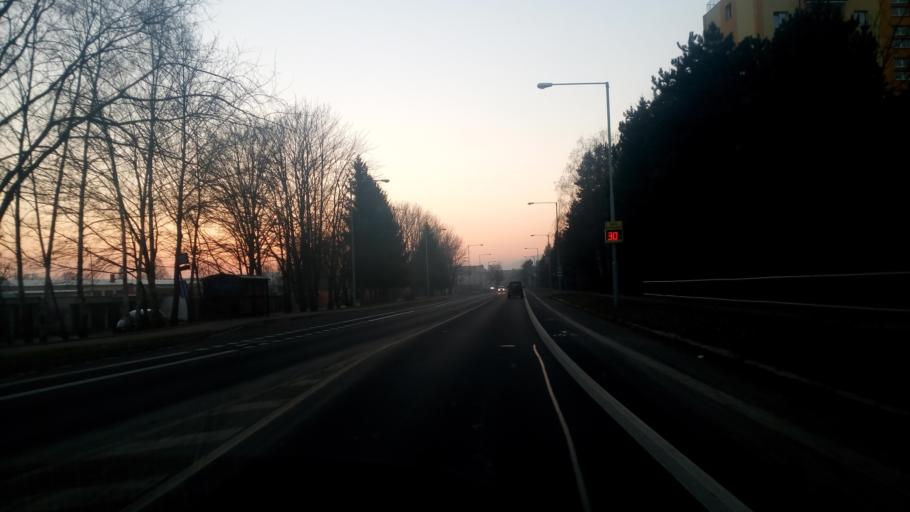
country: CZ
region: Olomoucky
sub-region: Okres Sumperk
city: Vikyrovice
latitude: 49.9653
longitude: 16.9944
